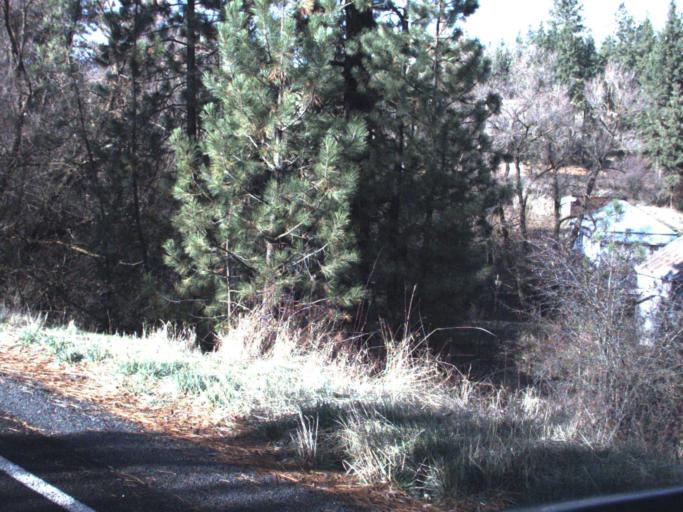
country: US
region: Washington
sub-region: Whitman County
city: Pullman
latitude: 46.9409
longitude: -117.1542
